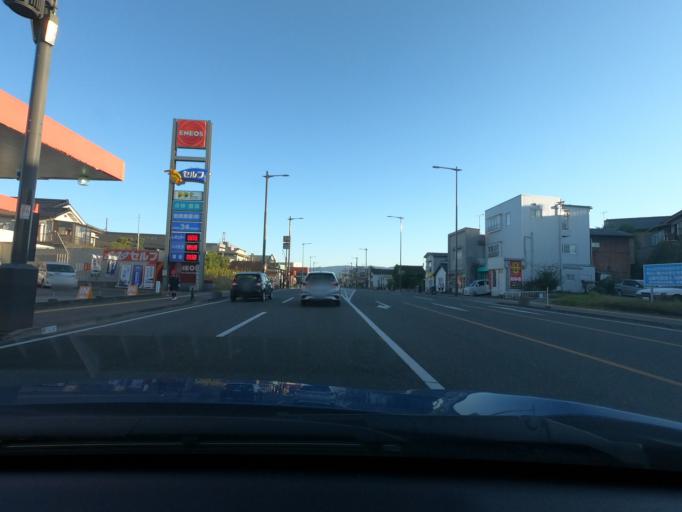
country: JP
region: Kagoshima
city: Satsumasendai
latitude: 31.8312
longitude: 130.2955
